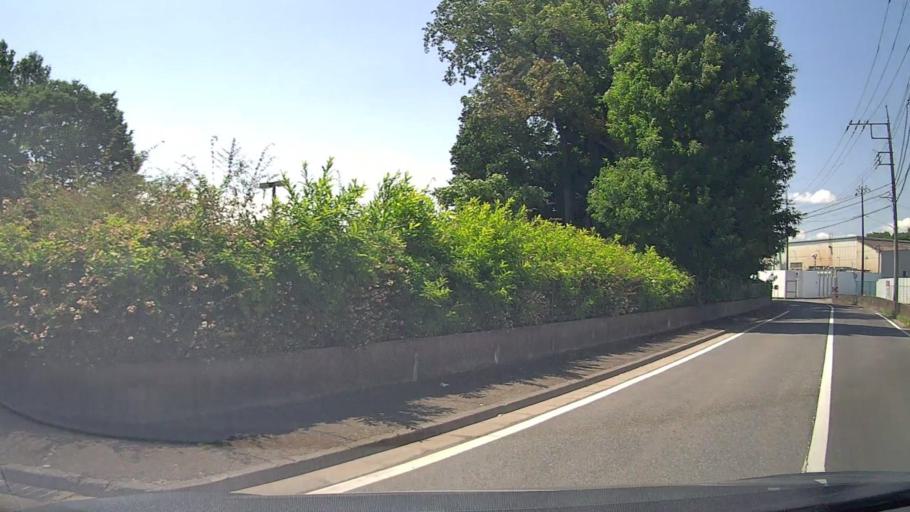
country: JP
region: Saitama
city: Tokorozawa
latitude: 35.8095
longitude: 139.4865
